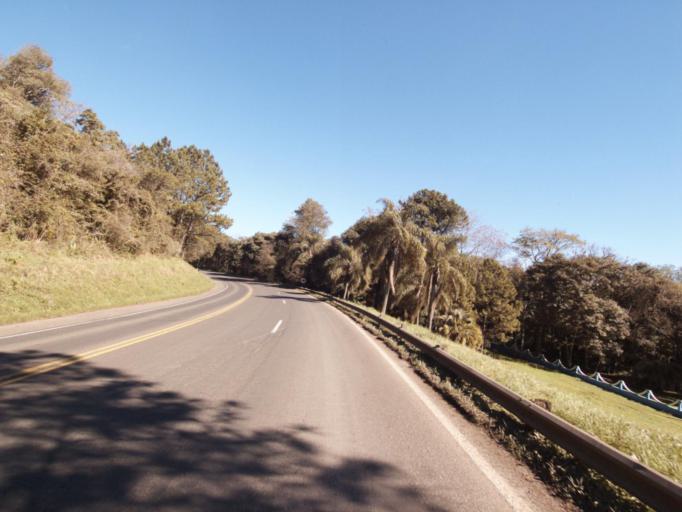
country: BR
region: Santa Catarina
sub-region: Joacaba
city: Joacaba
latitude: -27.1760
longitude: -51.5284
